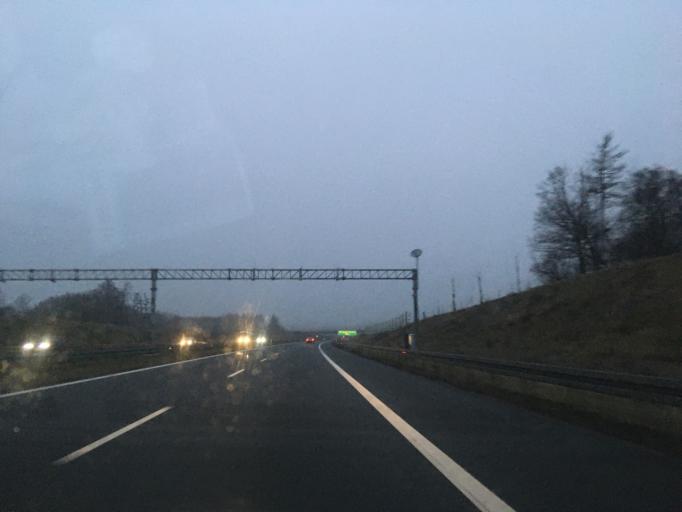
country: PL
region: Warmian-Masurian Voivodeship
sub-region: Powiat elblaski
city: Paslek
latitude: 54.0132
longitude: 19.6776
